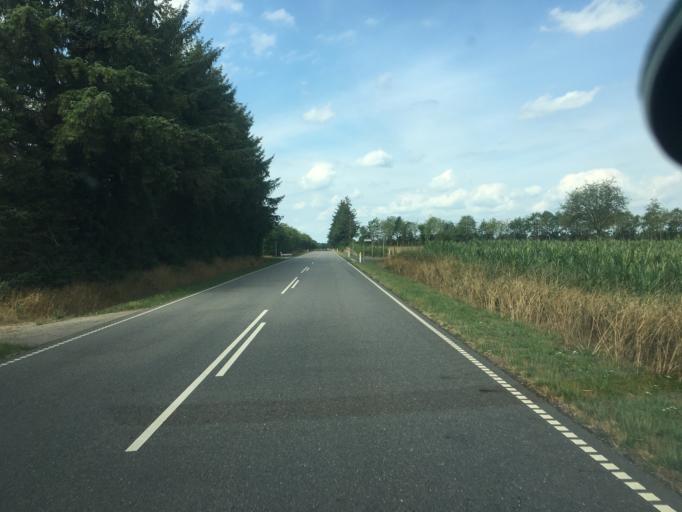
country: DK
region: South Denmark
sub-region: Aabenraa Kommune
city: Tinglev
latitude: 54.9364
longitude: 9.3177
